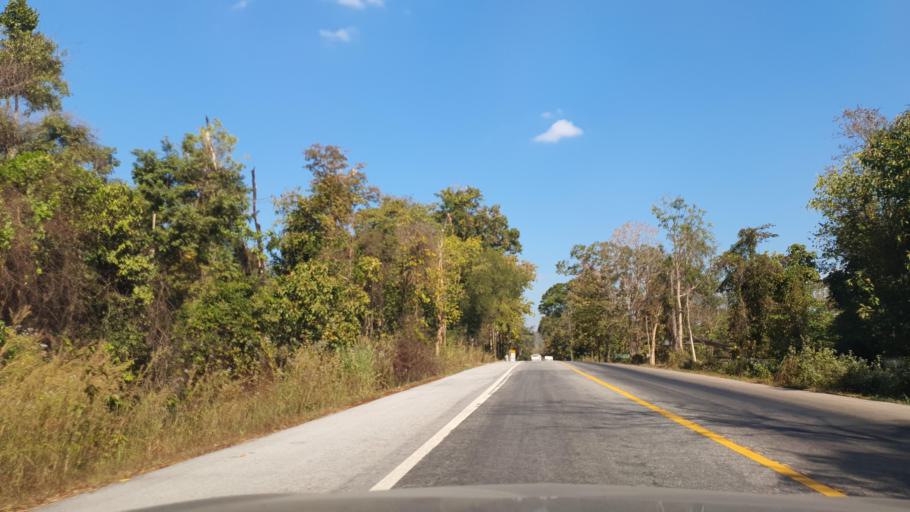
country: TH
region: Kalasin
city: Na Khu
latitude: 16.8502
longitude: 103.9272
